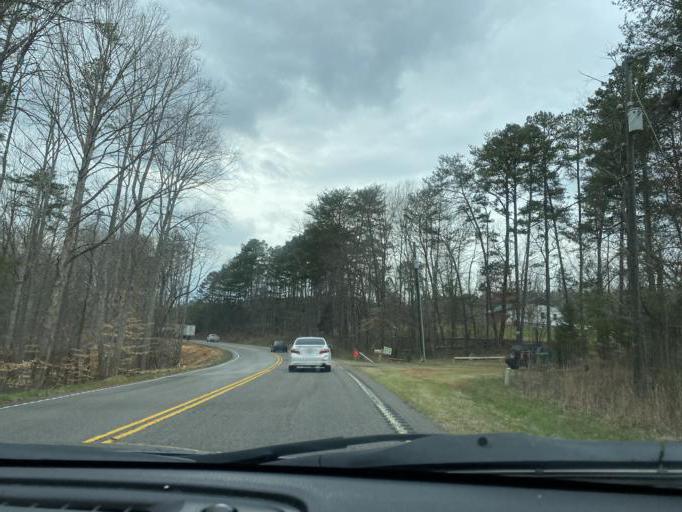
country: US
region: South Carolina
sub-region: Spartanburg County
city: Cowpens
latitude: 35.0171
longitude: -81.7439
